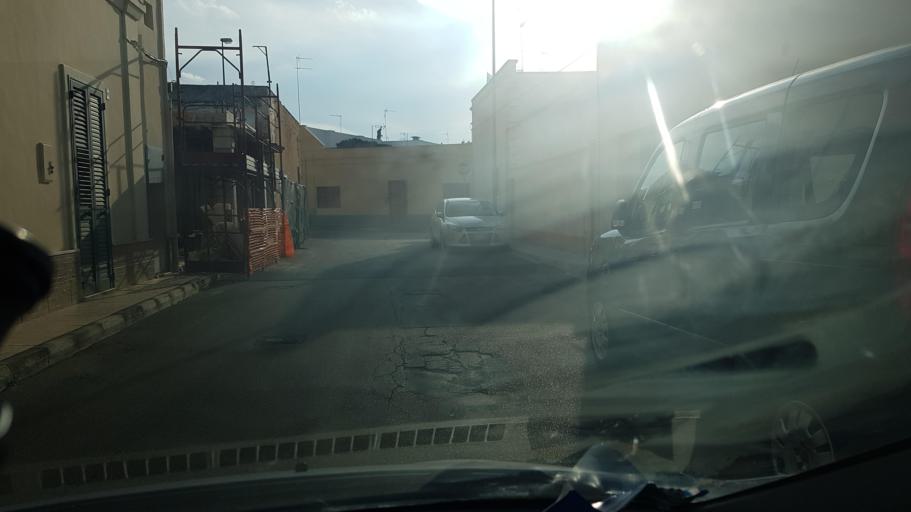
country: IT
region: Apulia
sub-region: Provincia di Lecce
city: Veglie
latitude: 40.3287
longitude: 17.9688
